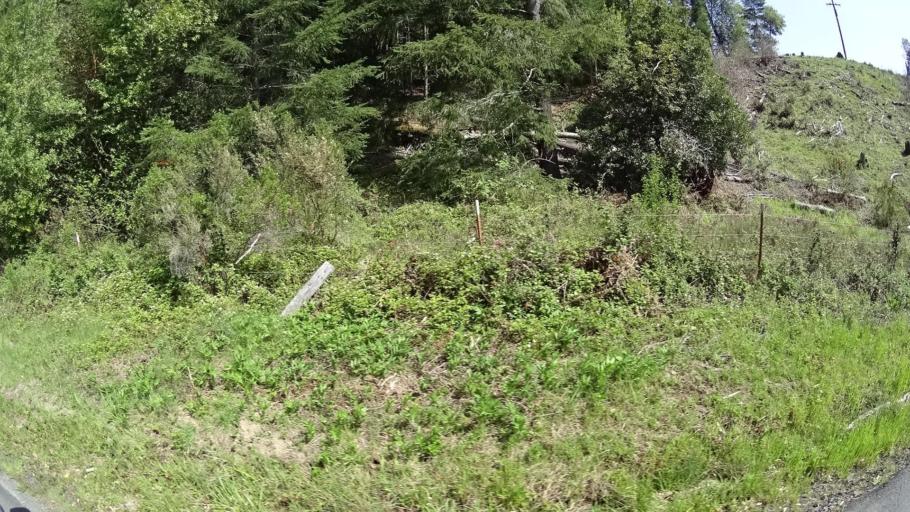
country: US
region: California
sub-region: Humboldt County
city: Redway
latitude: 40.3834
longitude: -123.7421
